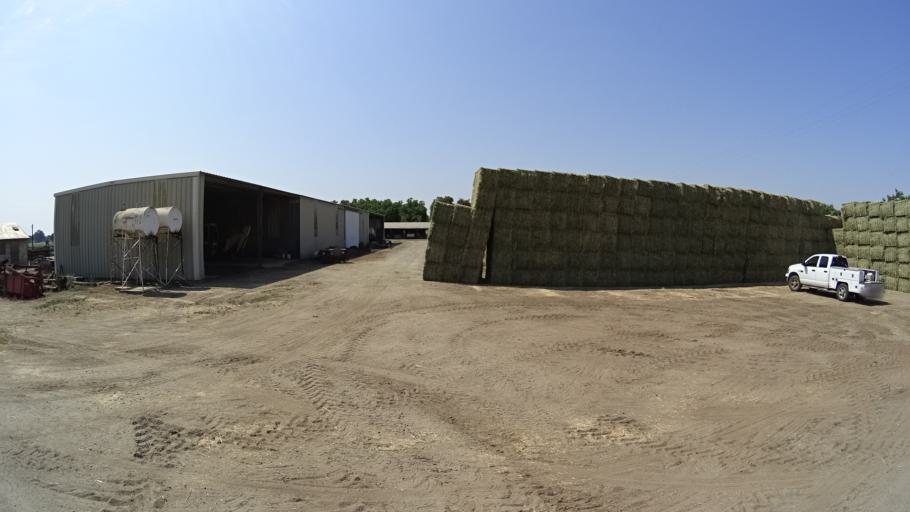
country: US
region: California
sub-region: Fresno County
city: Riverdale
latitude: 36.3948
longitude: -119.7813
